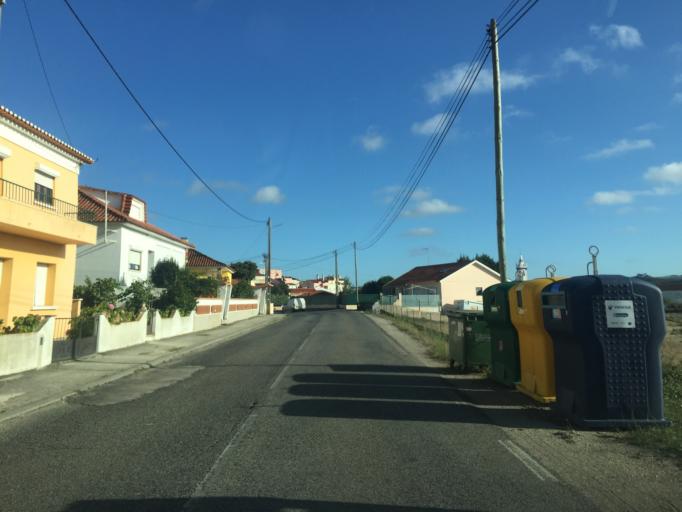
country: PT
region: Lisbon
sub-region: Torres Vedras
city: A dos Cunhados
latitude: 39.1555
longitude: -9.2996
